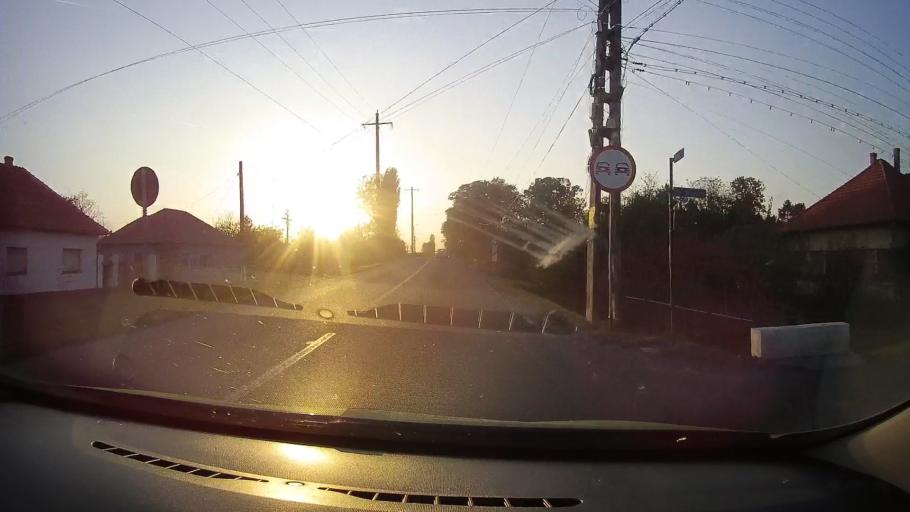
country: RO
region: Arad
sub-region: Comuna Ineu
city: Ineu
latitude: 46.4300
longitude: 21.8297
